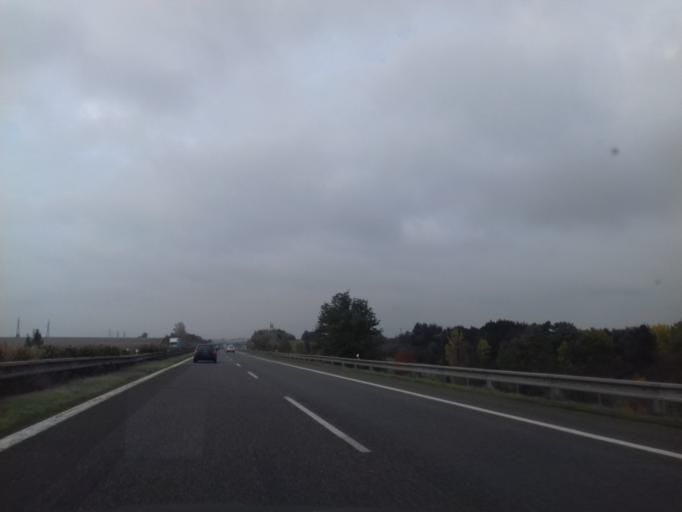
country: SK
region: Bratislavsky
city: Stupava
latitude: 48.2795
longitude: 17.0092
